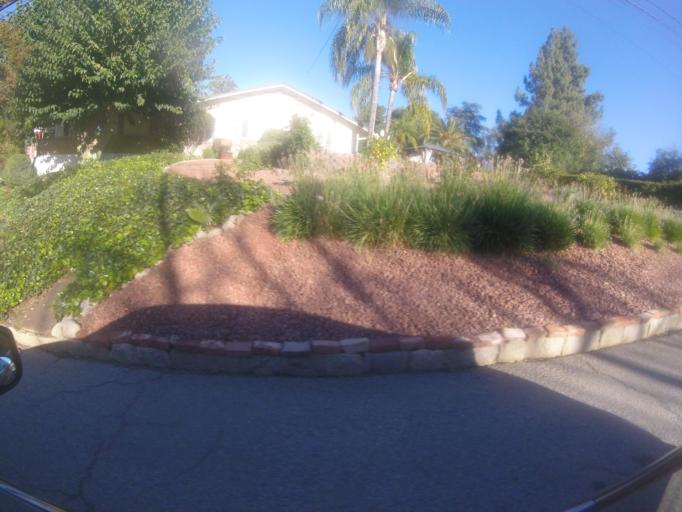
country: US
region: California
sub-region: San Bernardino County
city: Redlands
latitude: 34.0281
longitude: -117.1865
